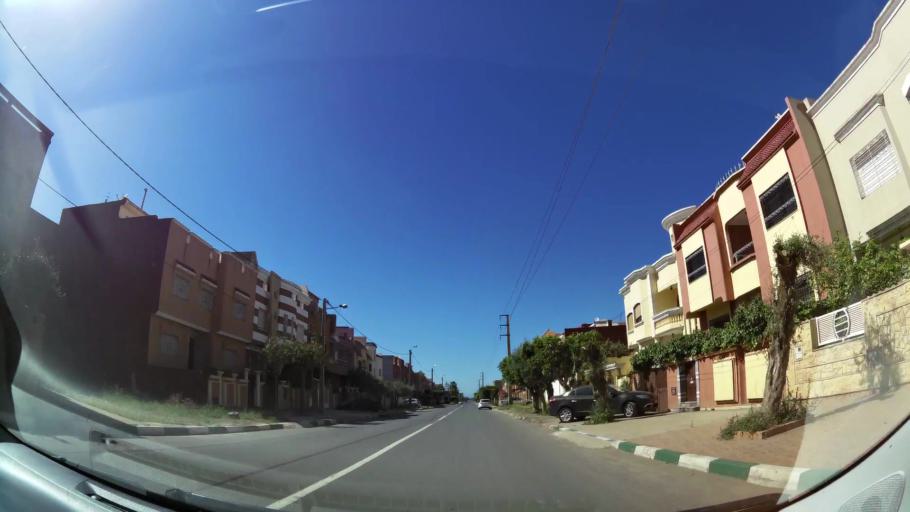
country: MA
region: Oriental
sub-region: Berkane-Taourirt
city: Berkane
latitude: 34.9380
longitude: -2.3242
